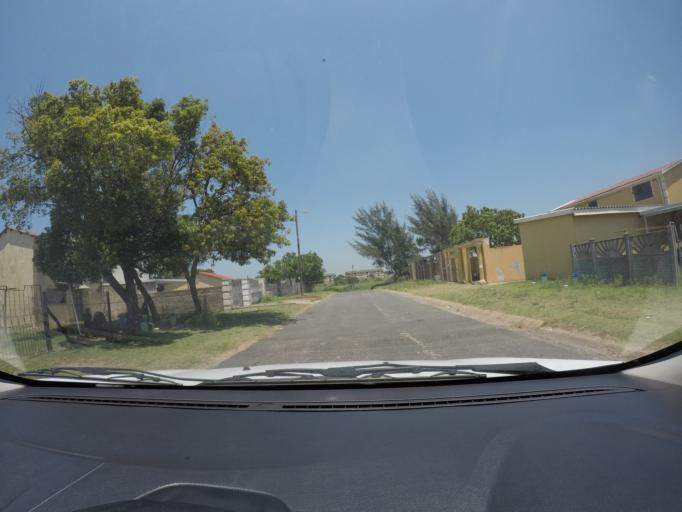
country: ZA
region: KwaZulu-Natal
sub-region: uThungulu District Municipality
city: eSikhawini
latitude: -28.8794
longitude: 31.9065
